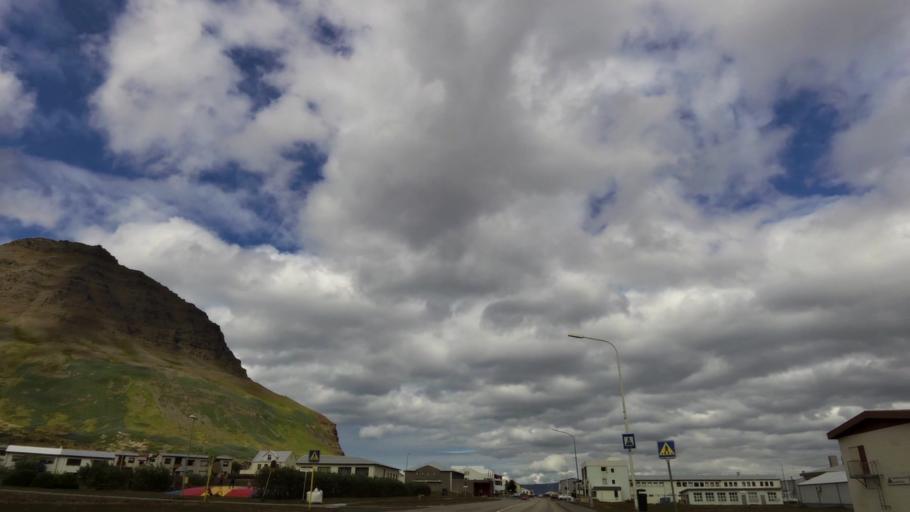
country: IS
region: Westfjords
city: Isafjoerdur
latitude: 66.1557
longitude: -23.2514
